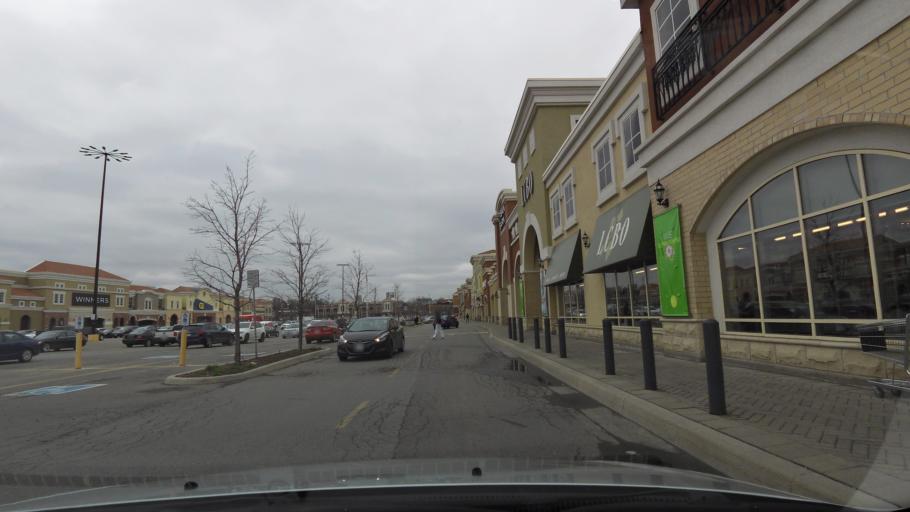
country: CA
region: Ontario
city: Toronto
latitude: 43.7107
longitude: -79.3601
